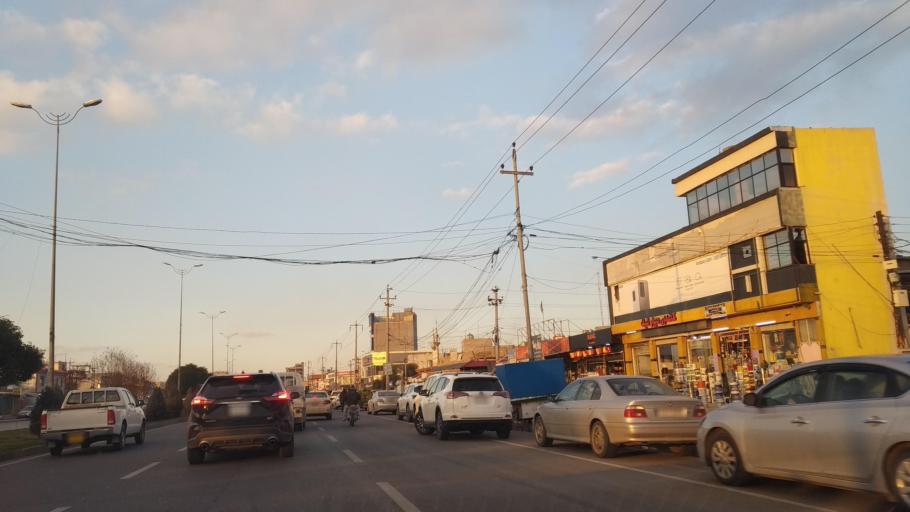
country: IQ
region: Arbil
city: Erbil
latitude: 36.1712
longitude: 44.0377
